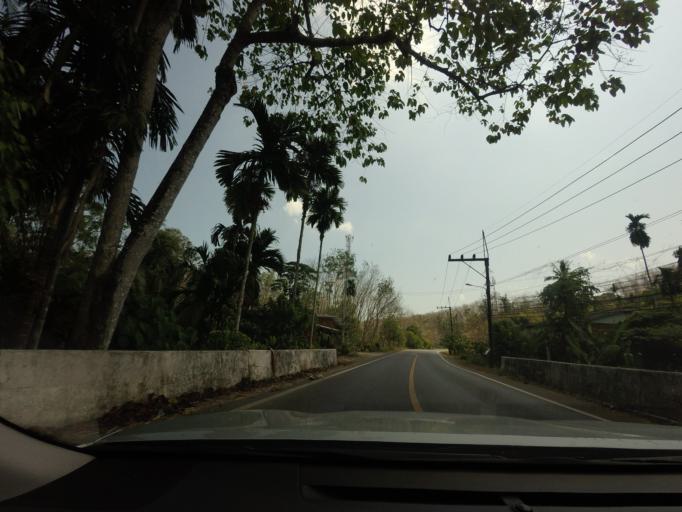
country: TH
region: Phangnga
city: Takua Thung
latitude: 8.2488
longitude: 98.3905
